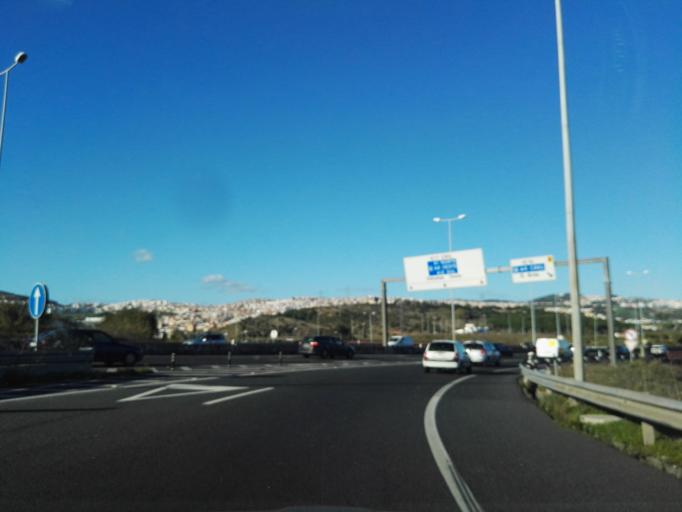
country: PT
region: Lisbon
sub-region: Odivelas
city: Pontinha
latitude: 38.7677
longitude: -9.2089
